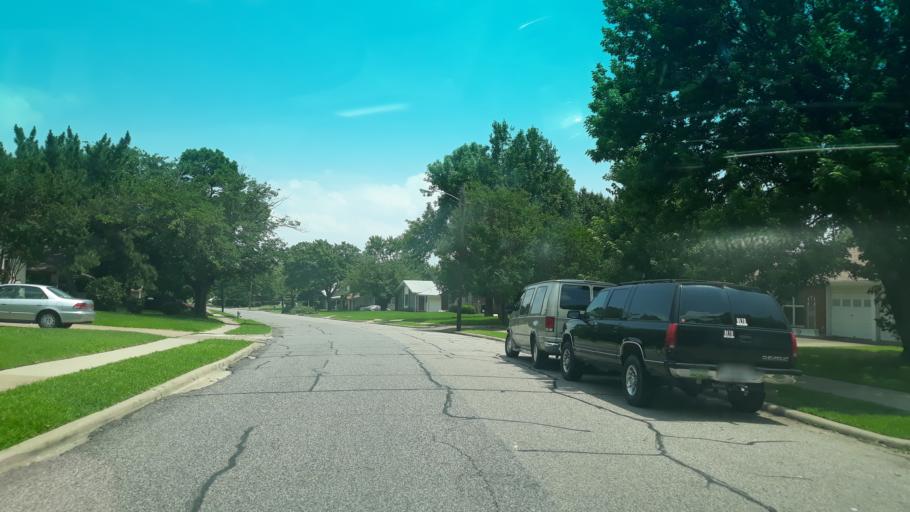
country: US
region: Texas
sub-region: Dallas County
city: Irving
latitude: 32.8559
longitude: -96.9632
